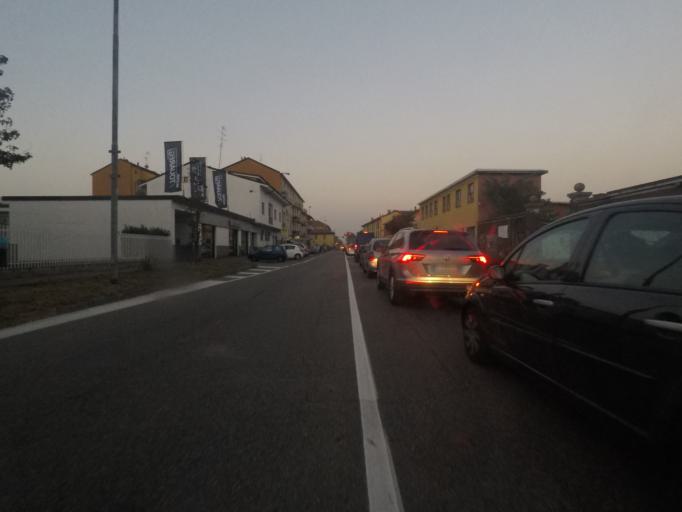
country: IT
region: Lombardy
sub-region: Citta metropolitana di Milano
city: Cologno Monzese
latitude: 45.5408
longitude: 9.2881
